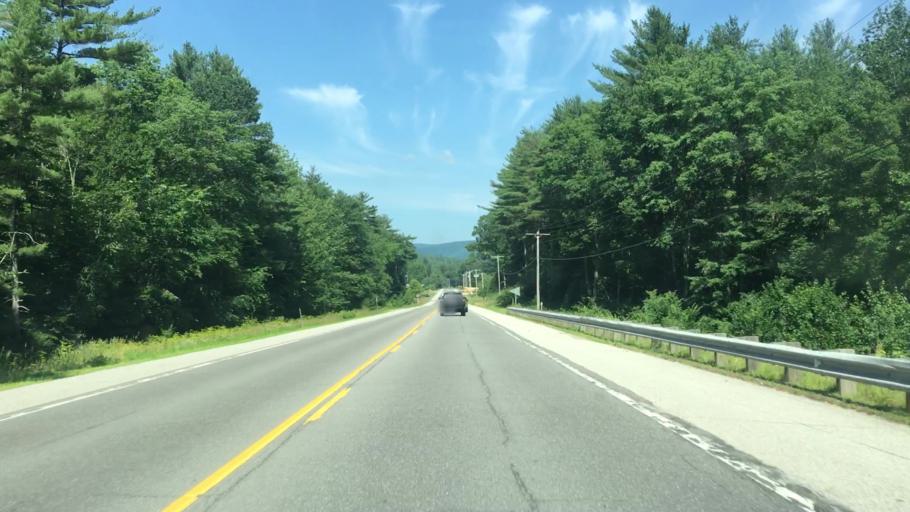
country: US
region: New Hampshire
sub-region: Merrimack County
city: Sutton
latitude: 43.2567
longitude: -71.9358
